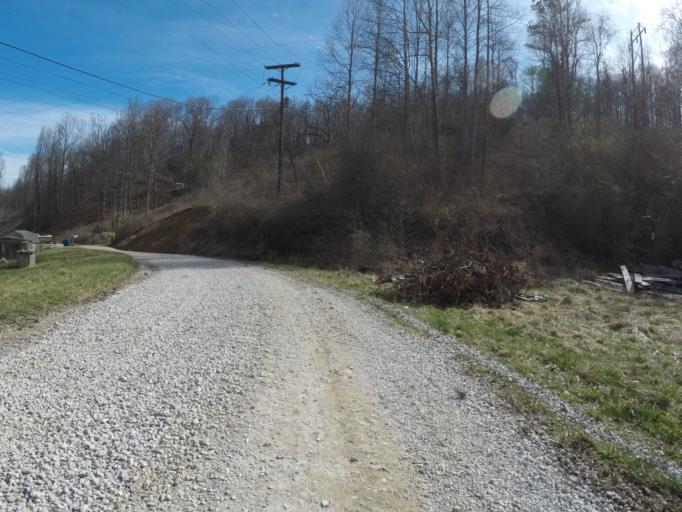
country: US
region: West Virginia
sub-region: Wayne County
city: Ceredo
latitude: 38.3453
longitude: -82.5478
